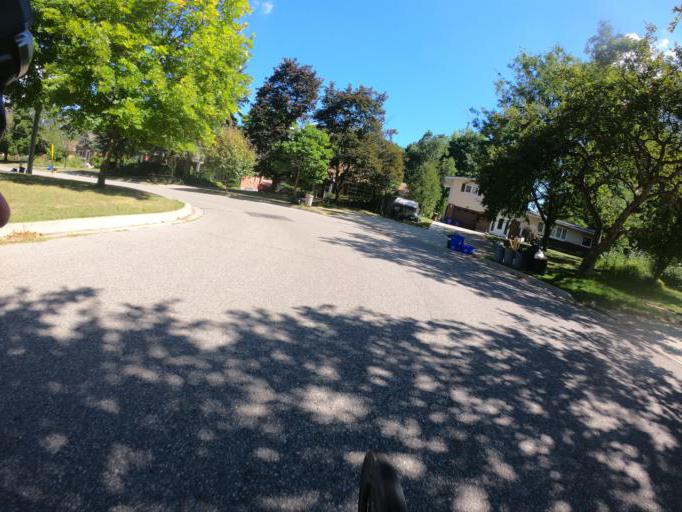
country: CA
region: Ontario
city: Waterloo
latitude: 43.4578
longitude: -80.5318
